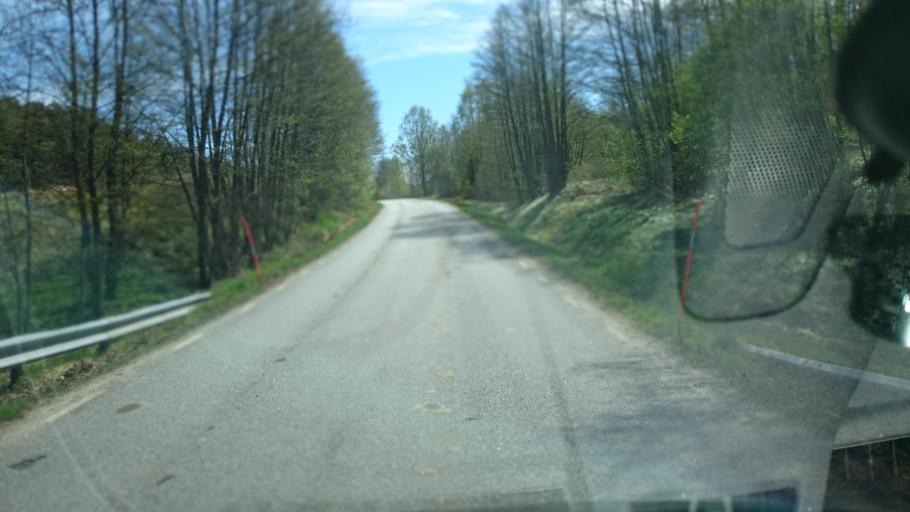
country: SE
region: Vaestra Goetaland
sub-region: Munkedals Kommun
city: Munkedal
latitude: 58.3746
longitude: 11.6836
